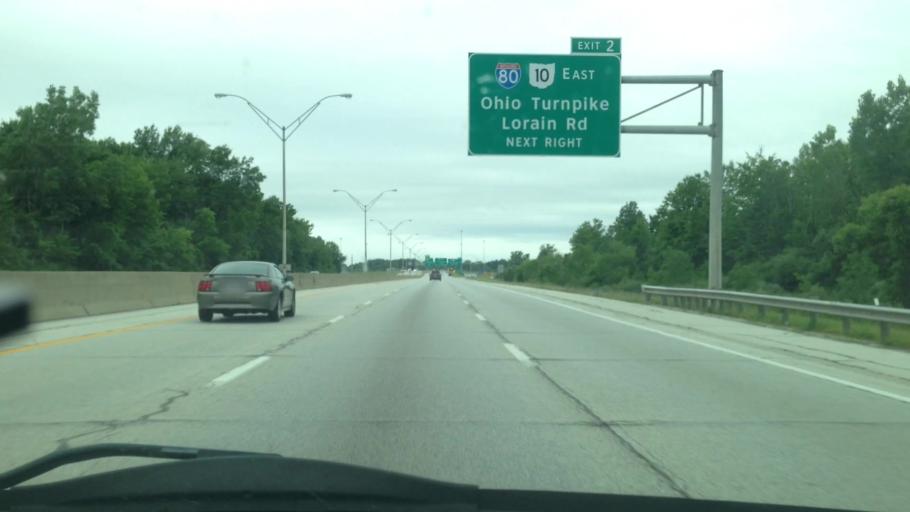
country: US
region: Ohio
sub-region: Cuyahoga County
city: North Olmsted
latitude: 41.3895
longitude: -81.9619
